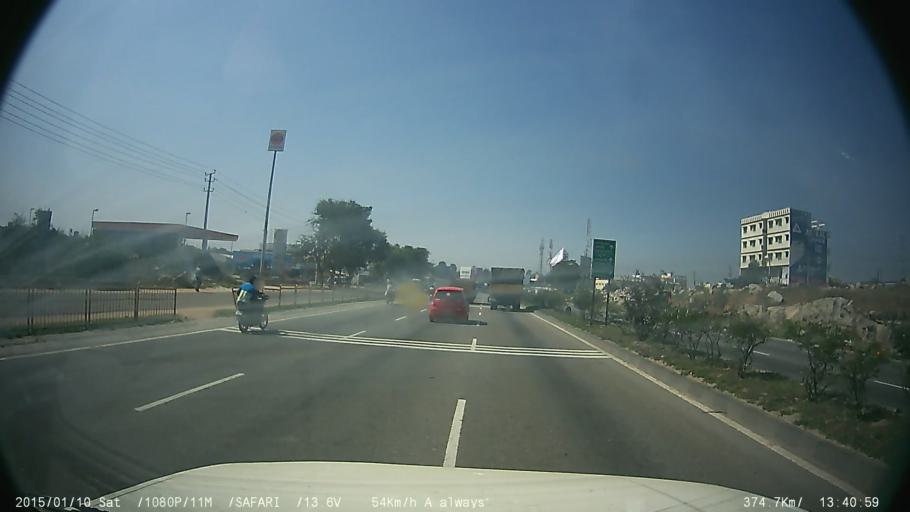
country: IN
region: Tamil Nadu
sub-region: Krishnagiri
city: Hosur
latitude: 12.7844
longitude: 77.7532
